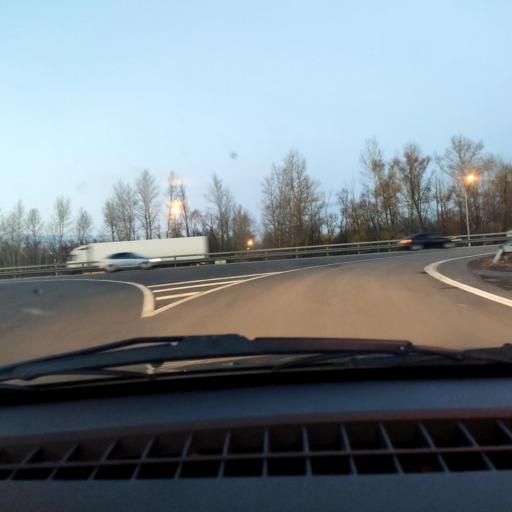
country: RU
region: Bashkortostan
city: Ufa
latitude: 54.6578
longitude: 55.8890
